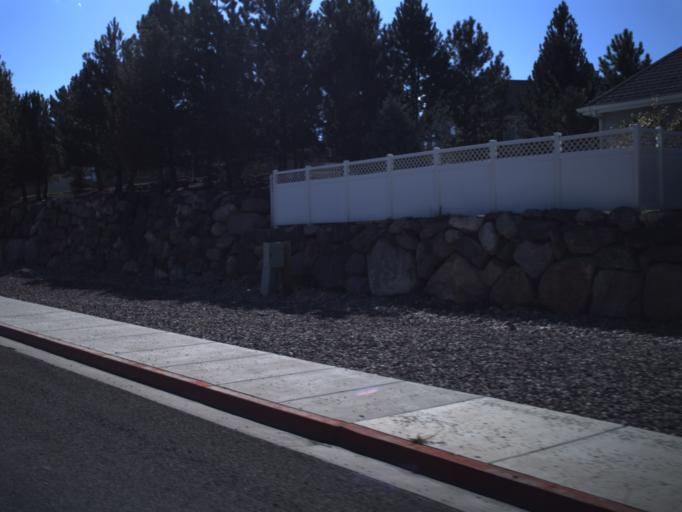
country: US
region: Utah
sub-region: Iron County
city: Cedar City
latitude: 37.6842
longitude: -113.0954
